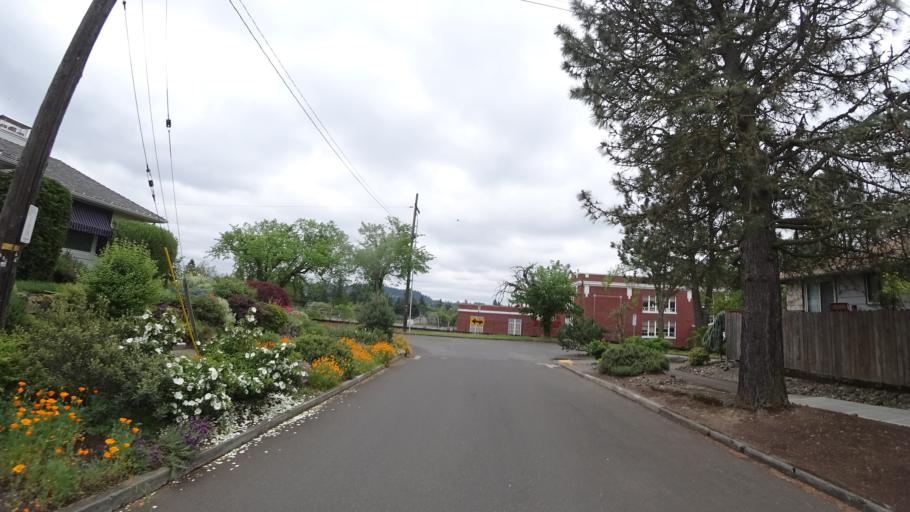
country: US
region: Oregon
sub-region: Multnomah County
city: Lents
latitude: 45.5402
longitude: -122.6036
